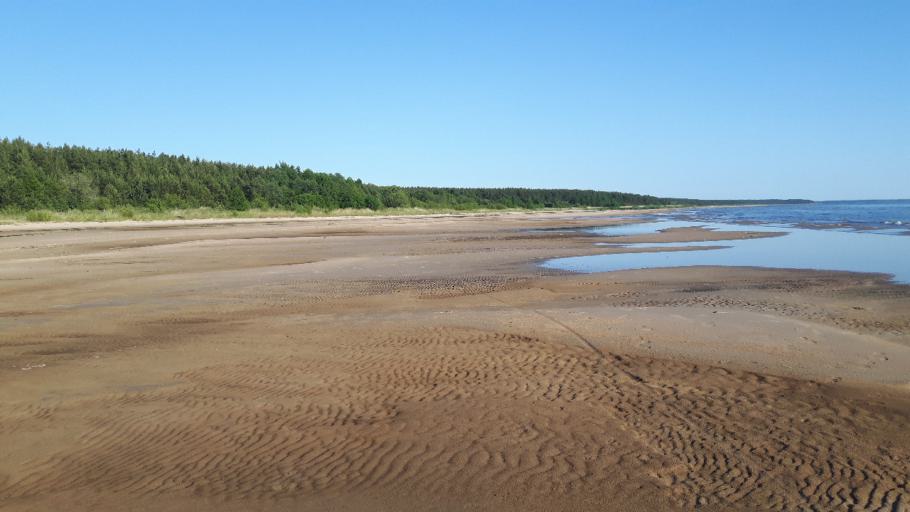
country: LV
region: Salacgrivas
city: Salacgriva
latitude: 57.6905
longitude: 24.3539
